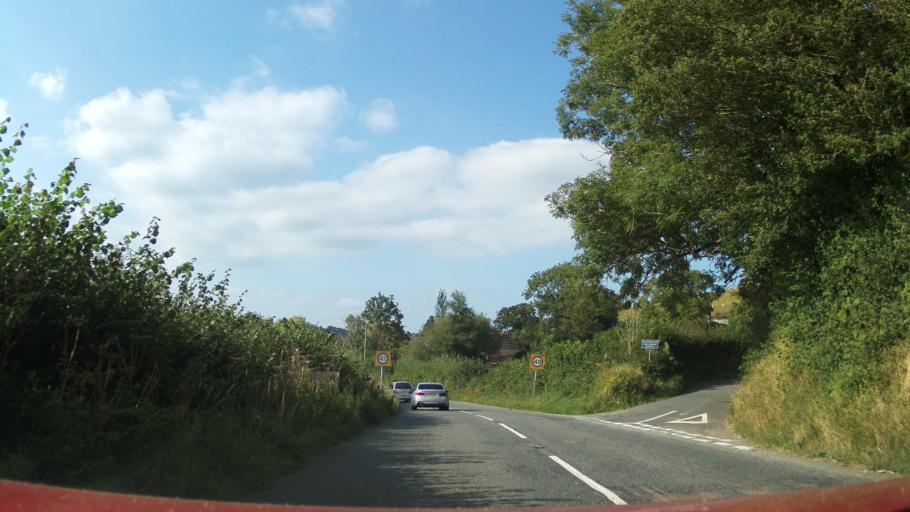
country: GB
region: England
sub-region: Devon
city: Tiverton
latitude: 50.8485
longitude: -3.5042
